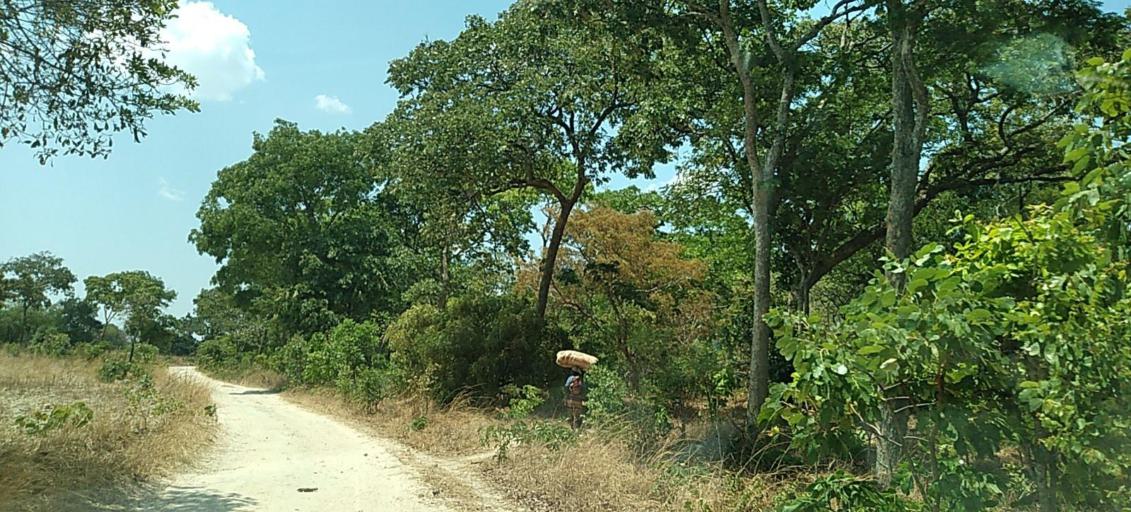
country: ZM
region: Central
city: Kapiri Mposhi
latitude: -13.6627
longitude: 28.4913
